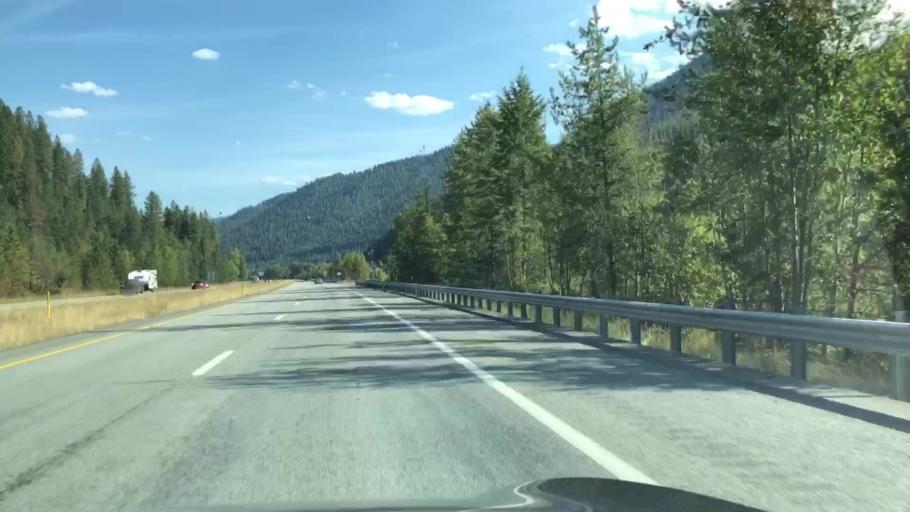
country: US
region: Idaho
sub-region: Shoshone County
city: Osburn
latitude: 47.5236
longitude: -116.0442
